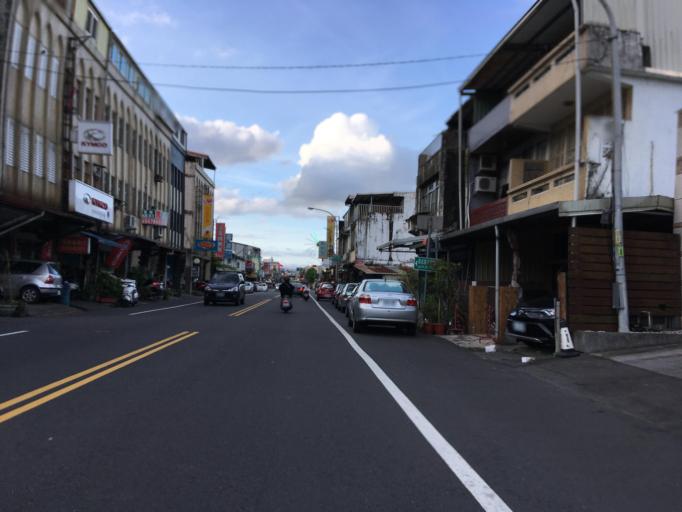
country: TW
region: Taiwan
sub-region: Yilan
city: Yilan
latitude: 24.6634
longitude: 121.7667
